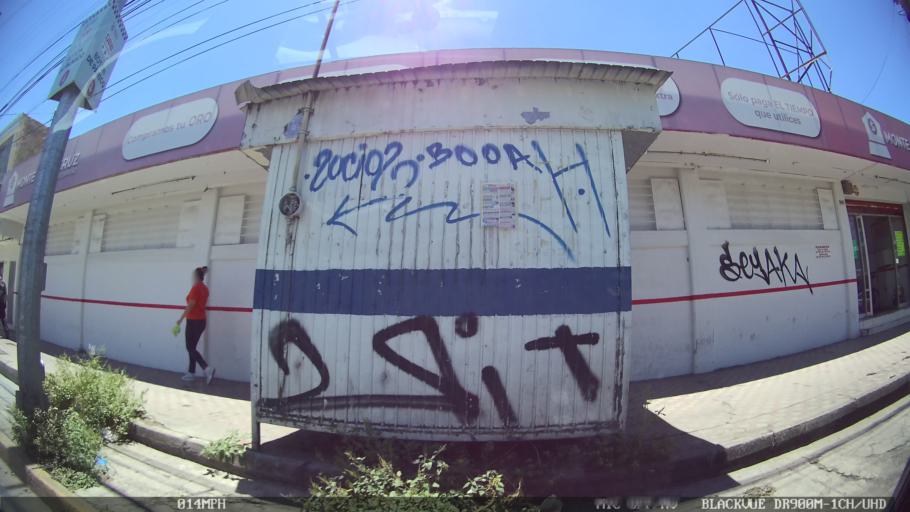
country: MX
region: Jalisco
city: Tlaquepaque
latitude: 20.6614
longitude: -103.2891
